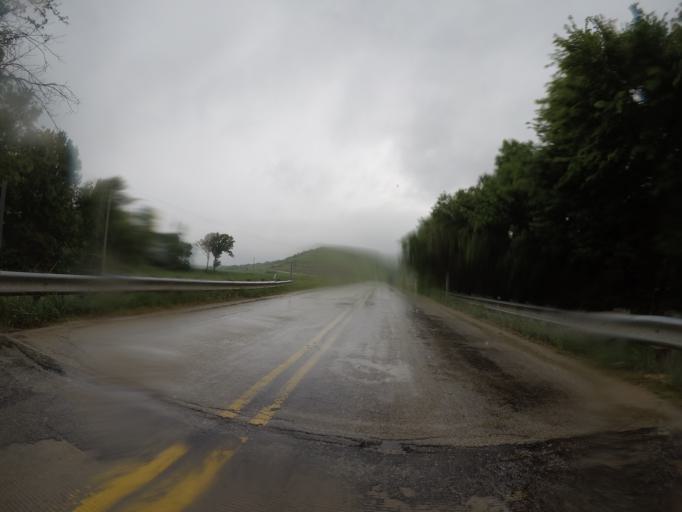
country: US
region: Kansas
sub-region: Pottawatomie County
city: Westmoreland
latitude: 39.3977
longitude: -96.1857
